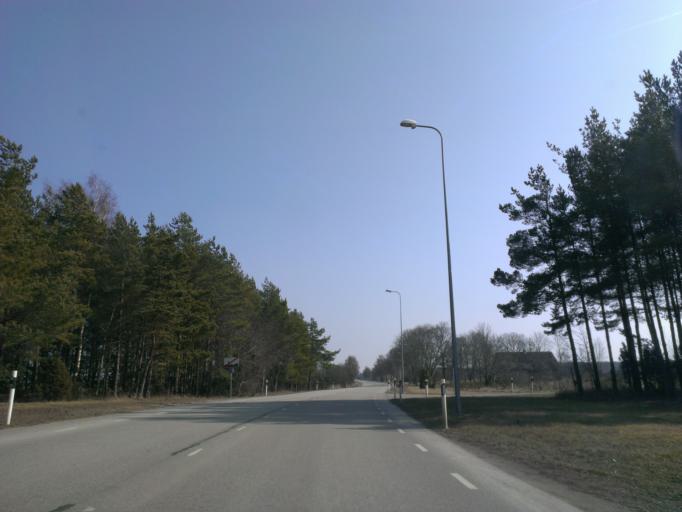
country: EE
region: Saare
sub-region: Orissaare vald
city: Orissaare
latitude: 58.5569
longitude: 23.0940
